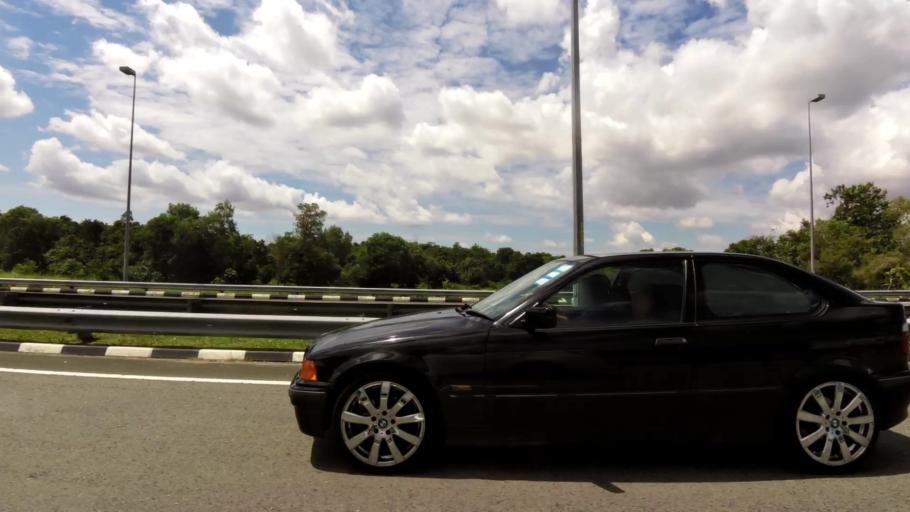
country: BN
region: Brunei and Muara
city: Bandar Seri Begawan
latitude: 4.9435
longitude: 114.9110
